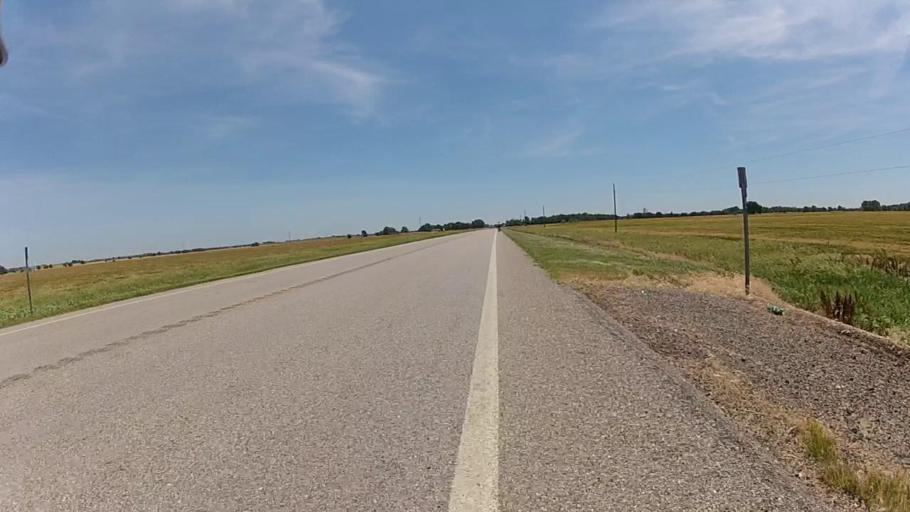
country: US
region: Kansas
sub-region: Barber County
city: Medicine Lodge
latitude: 37.2534
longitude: -98.4437
